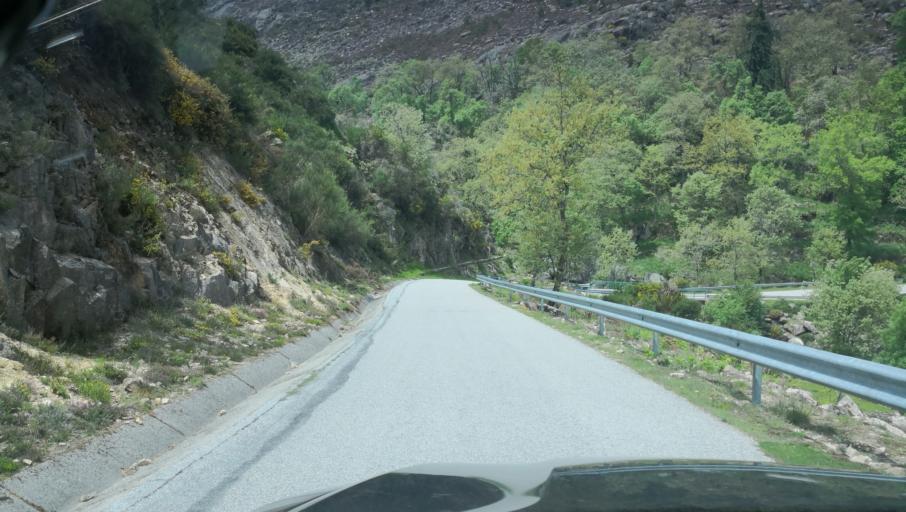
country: PT
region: Vila Real
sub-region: Vila Real
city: Vila Real
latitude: 41.3194
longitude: -7.7958
